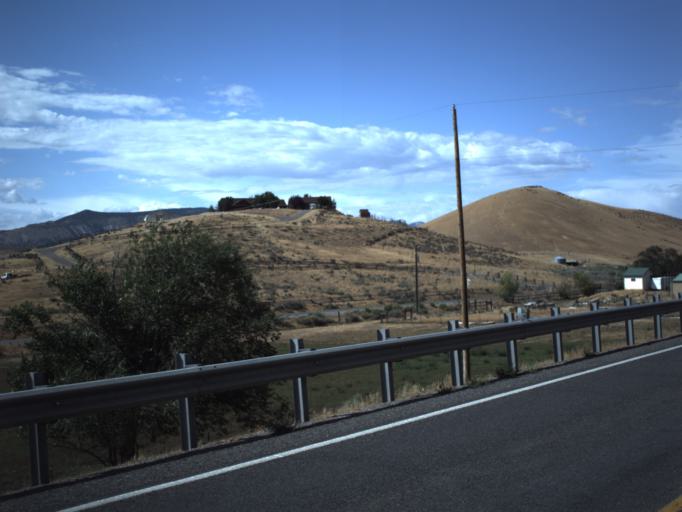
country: US
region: Utah
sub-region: Sanpete County
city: Manti
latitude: 39.2100
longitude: -111.6895
